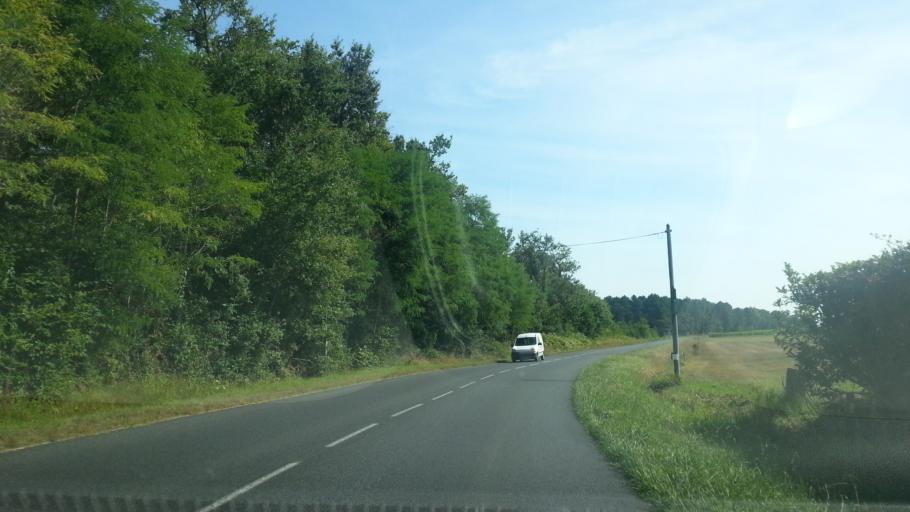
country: FR
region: Aquitaine
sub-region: Departement de la Gironde
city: Illats
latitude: 44.5863
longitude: -0.3947
